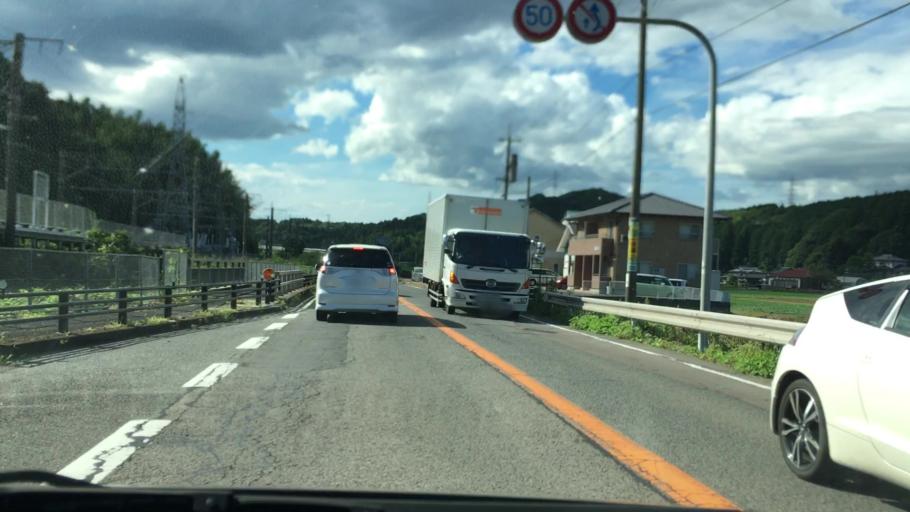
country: JP
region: Saga Prefecture
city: Takeocho-takeo
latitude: 33.1938
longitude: 129.9804
